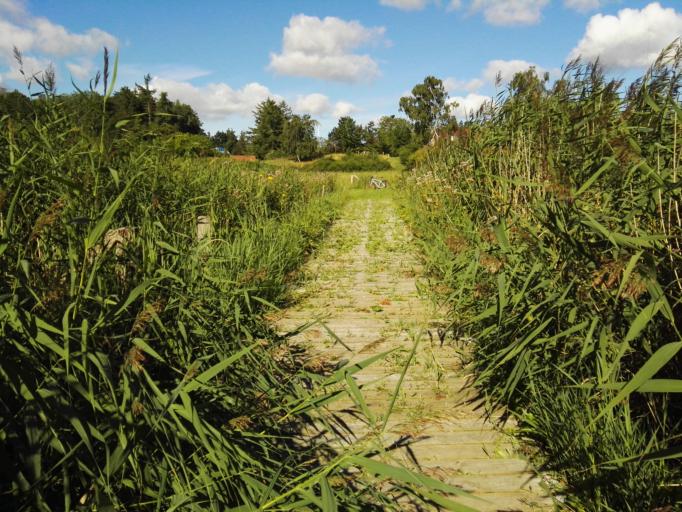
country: DK
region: Capital Region
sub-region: Frederikssund Kommune
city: Frederikssund
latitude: 55.7907
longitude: 12.0565
